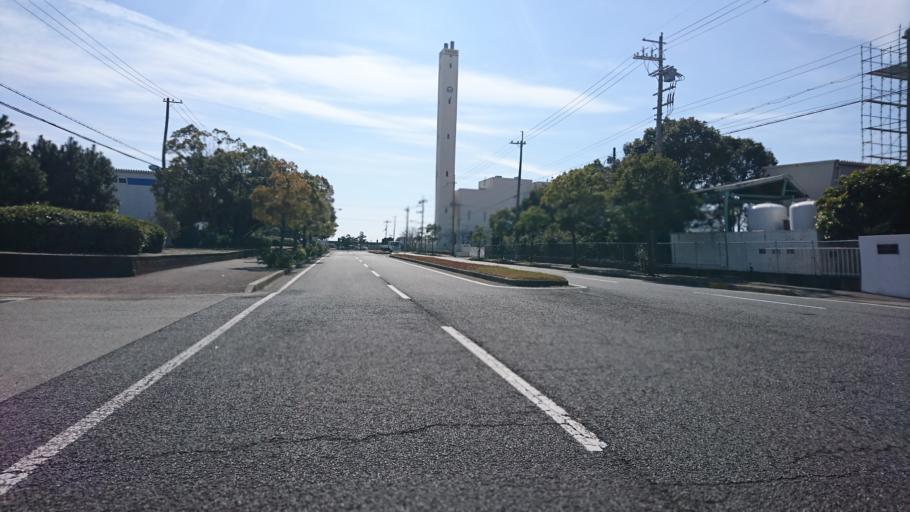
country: JP
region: Hyogo
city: Kakogawacho-honmachi
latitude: 34.6969
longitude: 134.8504
